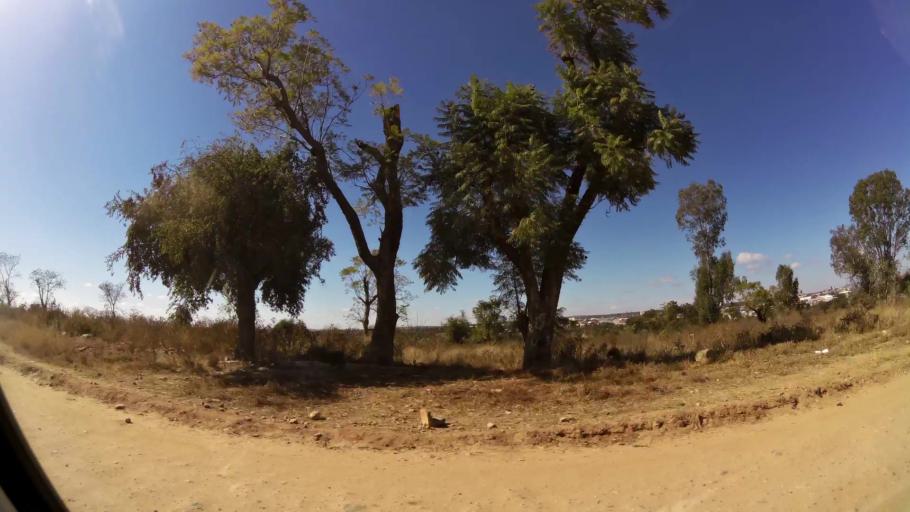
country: ZA
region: Limpopo
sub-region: Capricorn District Municipality
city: Polokwane
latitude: -23.8822
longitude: 29.4251
